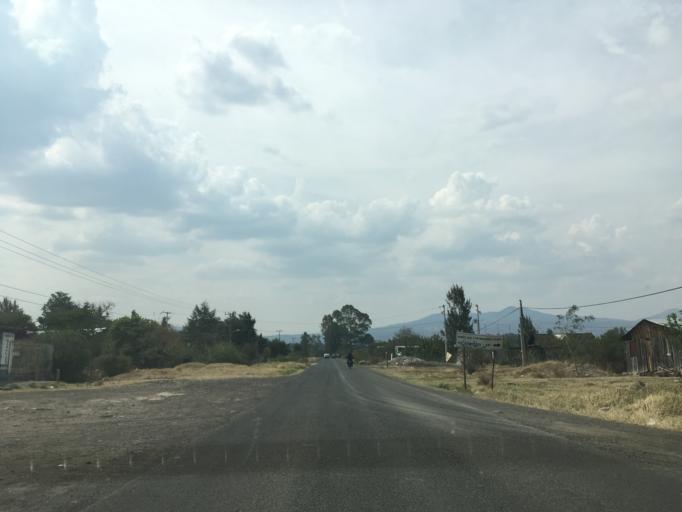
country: MX
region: Michoacan
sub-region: Morelia
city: La Mintzita (Piedra Dura)
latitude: 19.6452
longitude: -101.2792
